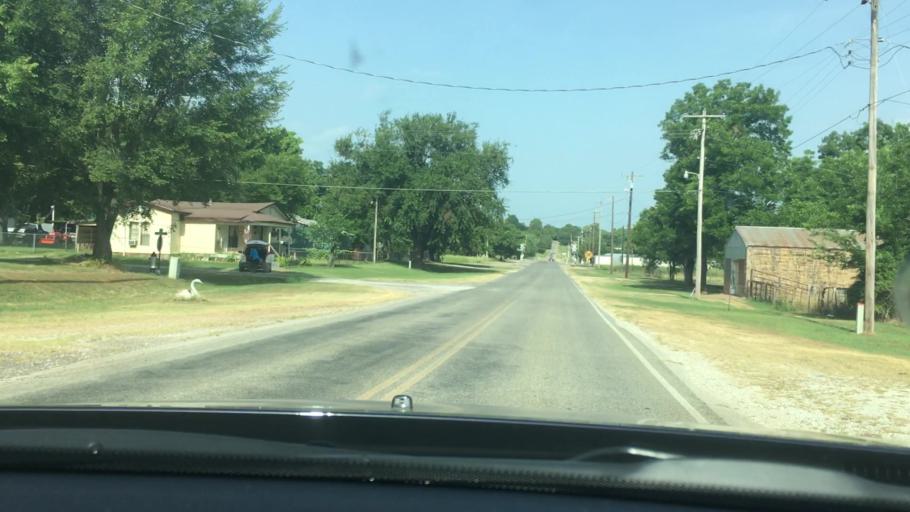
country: US
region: Oklahoma
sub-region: Pontotoc County
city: Byng
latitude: 34.8737
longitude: -96.5904
